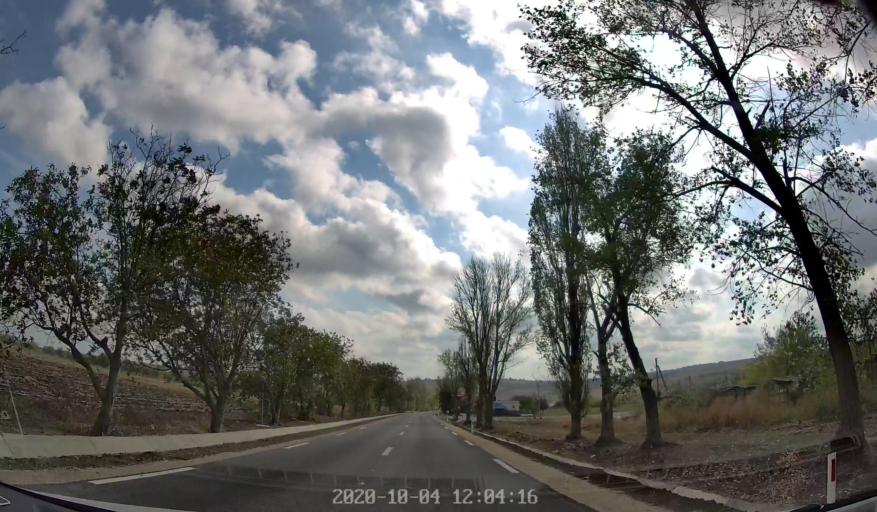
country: MD
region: Rezina
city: Saharna
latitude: 47.6052
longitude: 28.9406
